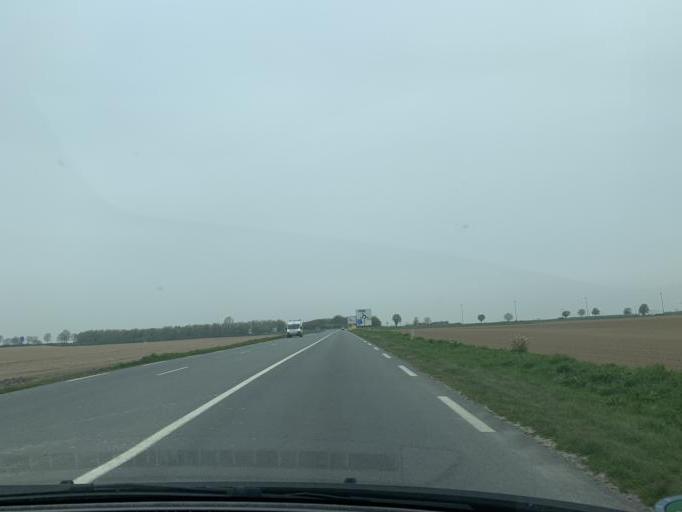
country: FR
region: Picardie
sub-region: Departement de la Somme
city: Abbeville
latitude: 50.1276
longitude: 1.8286
